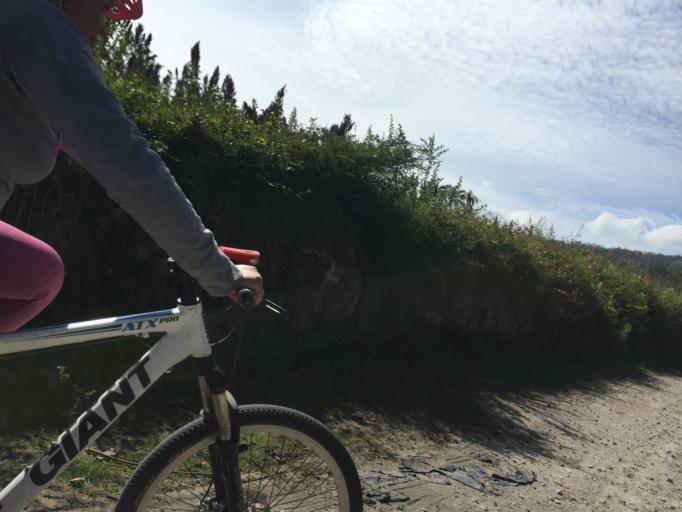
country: EC
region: Imbabura
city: Ibarra
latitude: 0.3125
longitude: -78.1482
